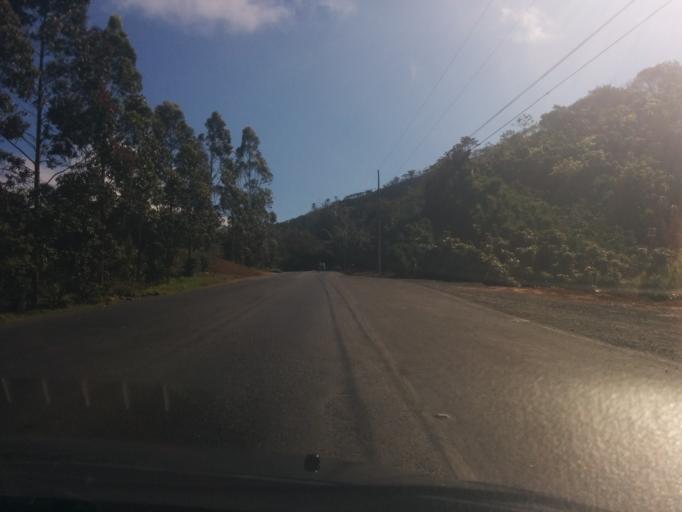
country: CR
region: Alajuela
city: San Rafael
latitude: 10.0557
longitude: -84.5023
